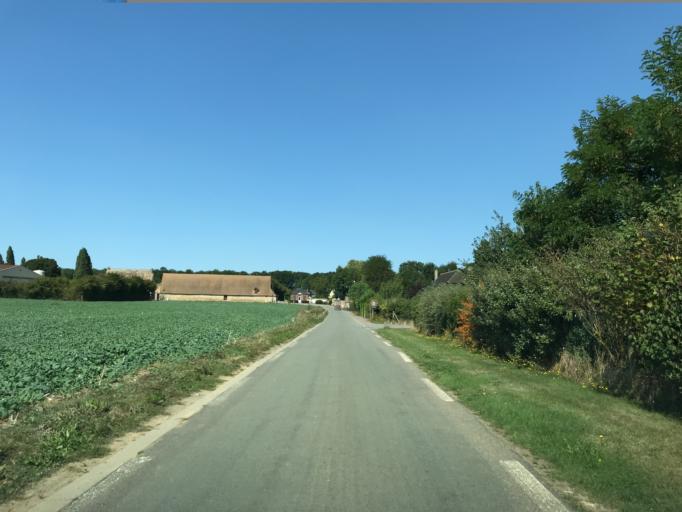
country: FR
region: Haute-Normandie
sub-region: Departement de l'Eure
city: Saint-Aubin-sur-Gaillon
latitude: 49.0731
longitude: 1.2656
